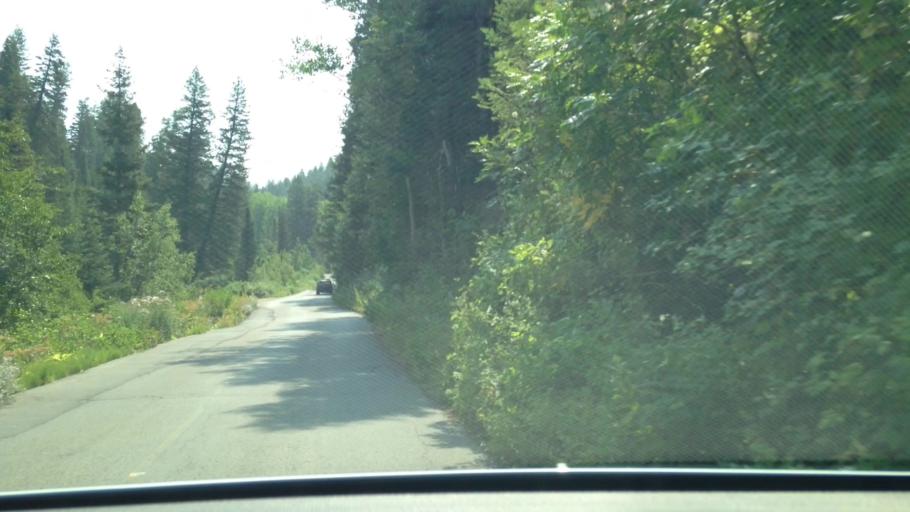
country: US
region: Utah
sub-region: Summit County
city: Summit Park
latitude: 40.6998
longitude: -111.6861
